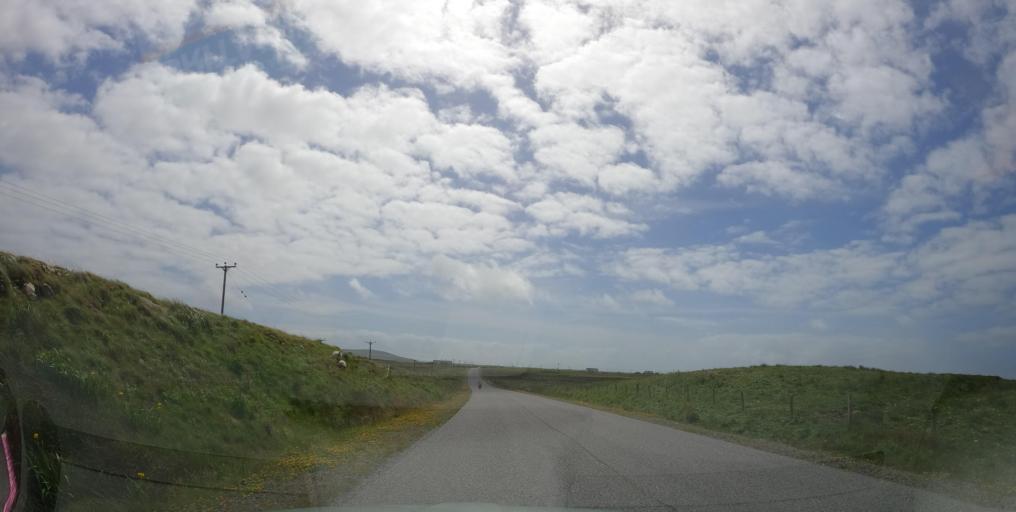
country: GB
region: Scotland
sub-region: Eilean Siar
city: Isle of South Uist
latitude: 57.2291
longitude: -7.3971
